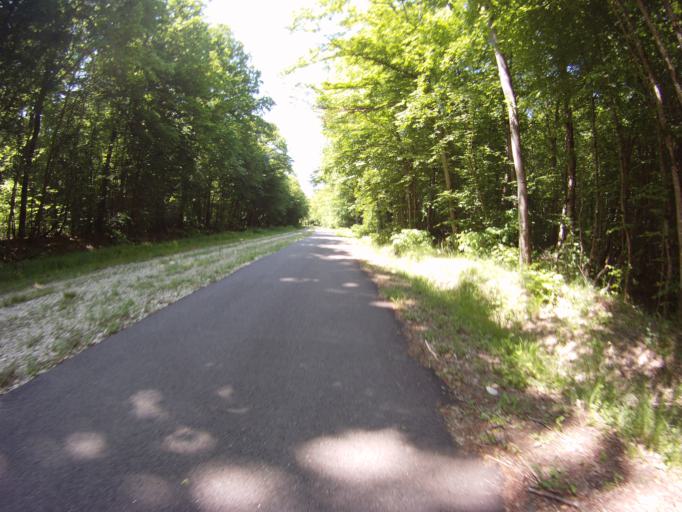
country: FR
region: Lorraine
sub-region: Departement de Meurthe-et-Moselle
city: Champenoux
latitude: 48.7586
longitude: 6.3371
